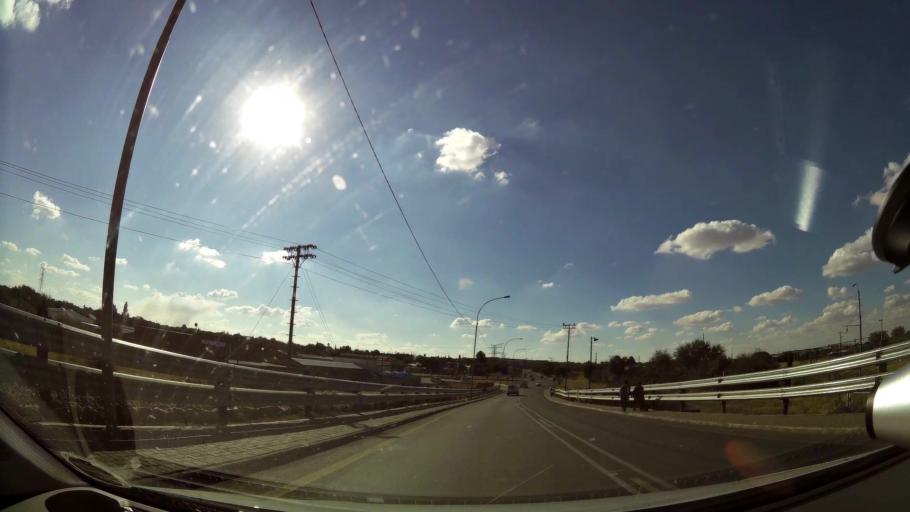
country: ZA
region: Northern Cape
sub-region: Frances Baard District Municipality
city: Kimberley
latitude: -28.7735
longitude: 24.7647
